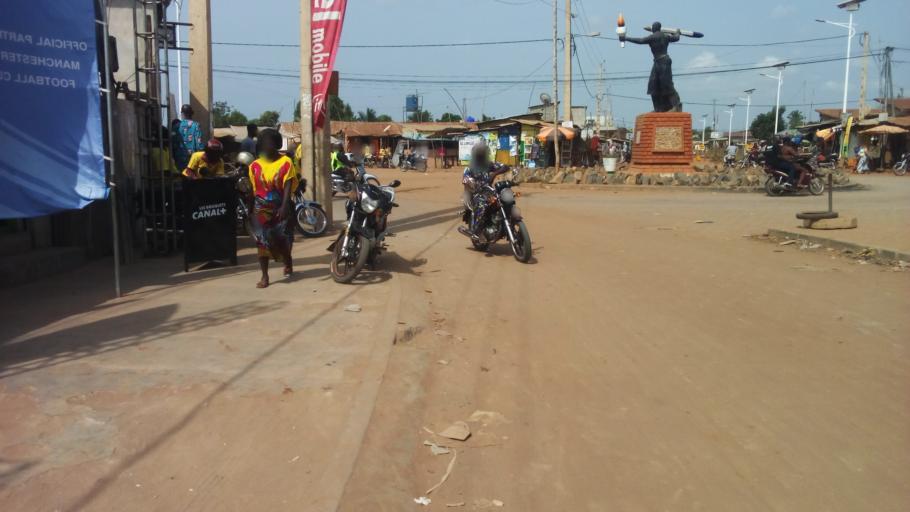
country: BJ
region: Atlantique
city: Abomey-Calavi
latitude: 6.4243
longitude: 2.3208
